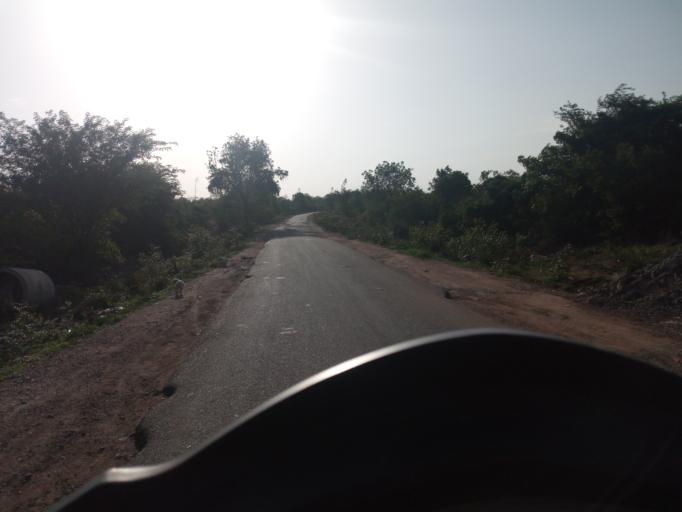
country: IN
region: Telangana
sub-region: Rangareddi
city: Quthbullapur
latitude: 17.5549
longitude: 78.4145
